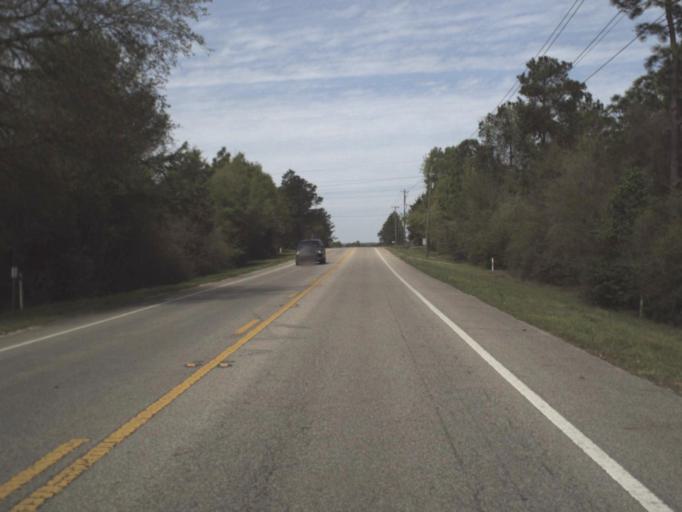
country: US
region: Florida
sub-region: Okaloosa County
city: Crestview
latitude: 30.7521
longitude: -86.4886
